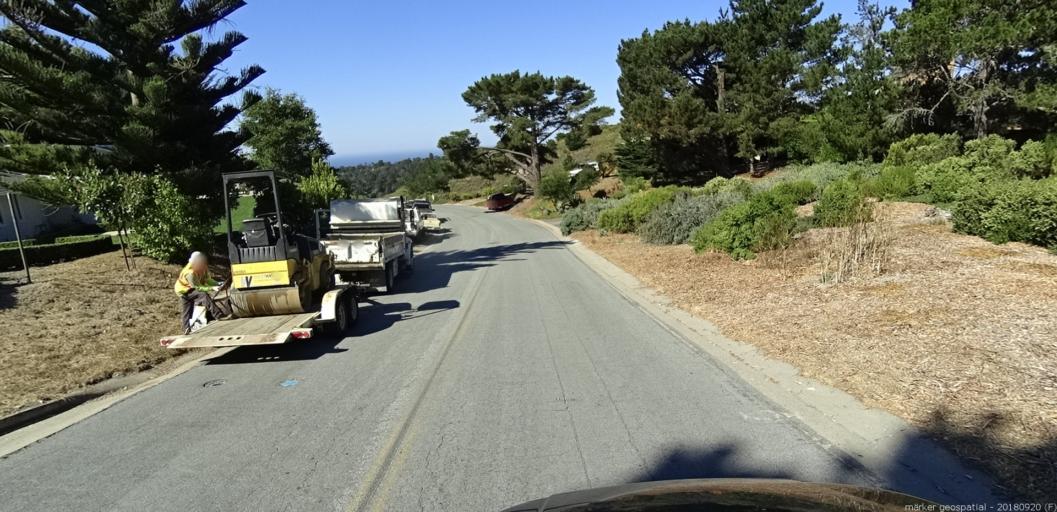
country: US
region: California
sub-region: Monterey County
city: Carmel-by-the-Sea
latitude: 36.5608
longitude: -121.8997
